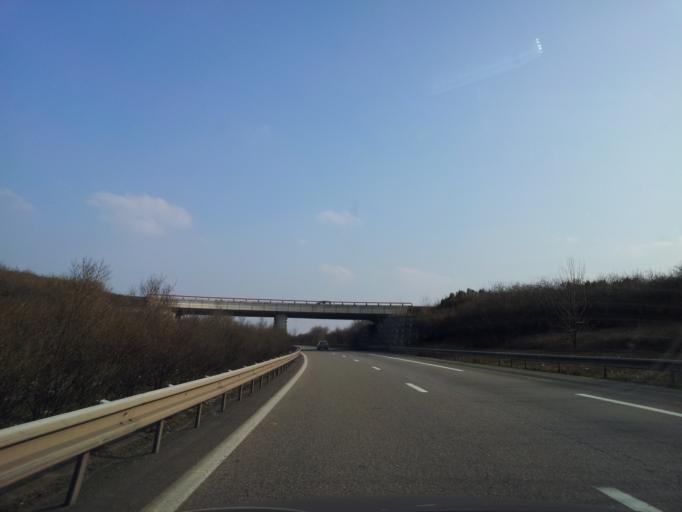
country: FR
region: Alsace
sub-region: Departement du Haut-Rhin
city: Houssen
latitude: 48.1201
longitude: 7.3671
